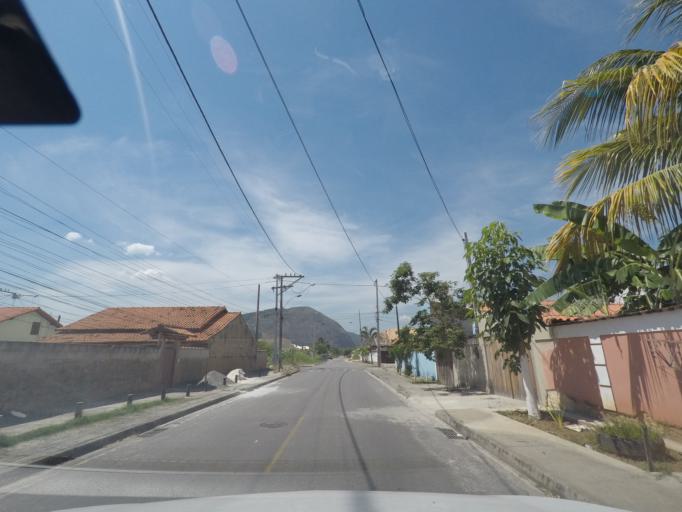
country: BR
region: Rio de Janeiro
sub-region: Marica
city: Marica
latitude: -22.9625
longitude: -42.9585
